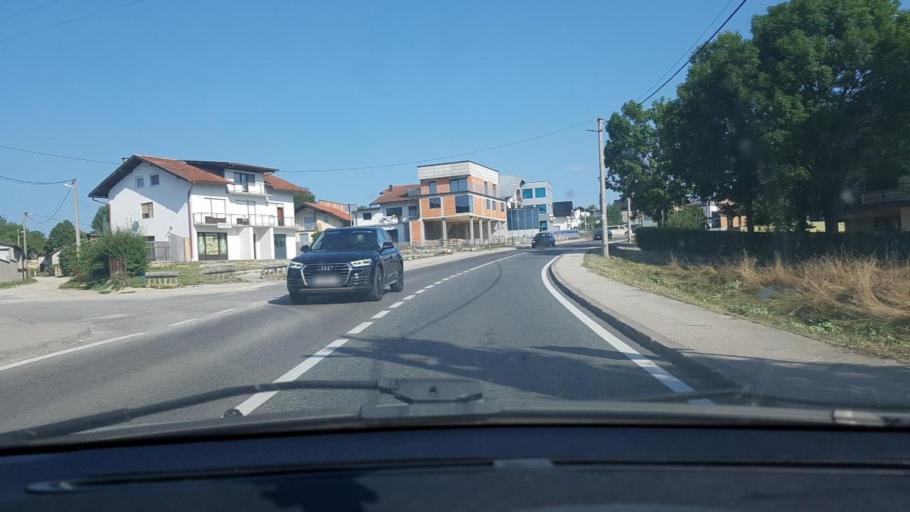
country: BA
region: Federation of Bosnia and Herzegovina
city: Ostrozac
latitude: 44.9089
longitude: 15.9321
